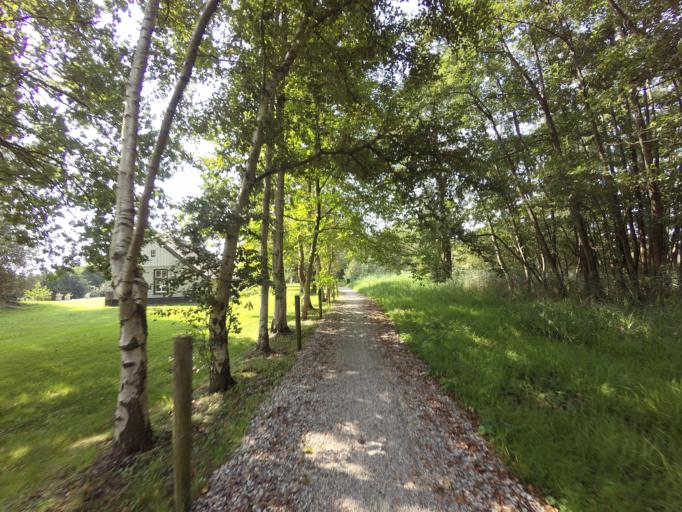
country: NL
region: Overijssel
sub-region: Gemeente Steenwijkerland
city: Oldemarkt
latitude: 52.8505
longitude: 5.9010
